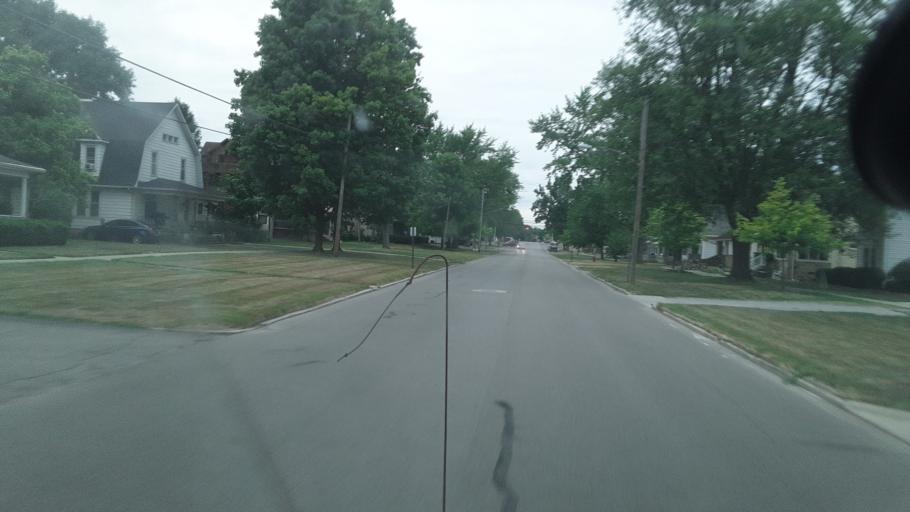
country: US
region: Ohio
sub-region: Defiance County
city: Hicksville
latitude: 41.2908
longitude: -84.7598
